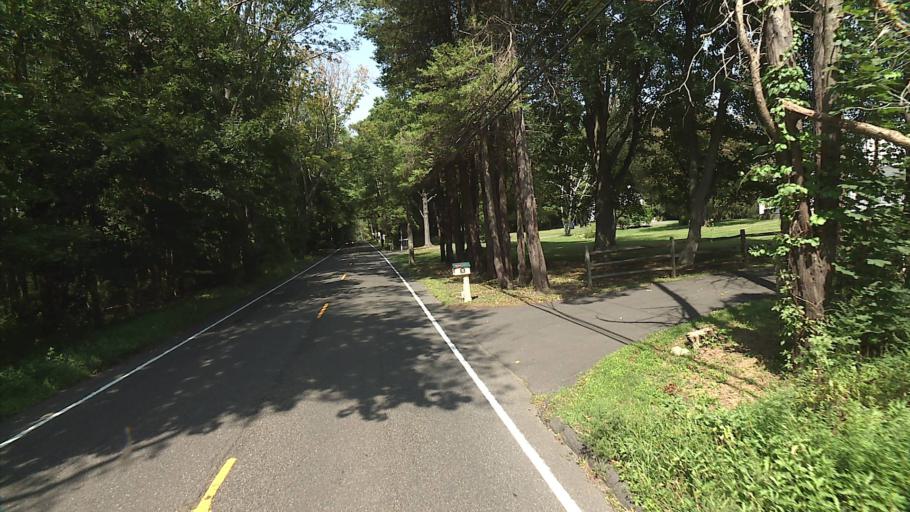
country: US
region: Connecticut
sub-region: Fairfield County
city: Georgetown
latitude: 41.2867
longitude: -73.3427
